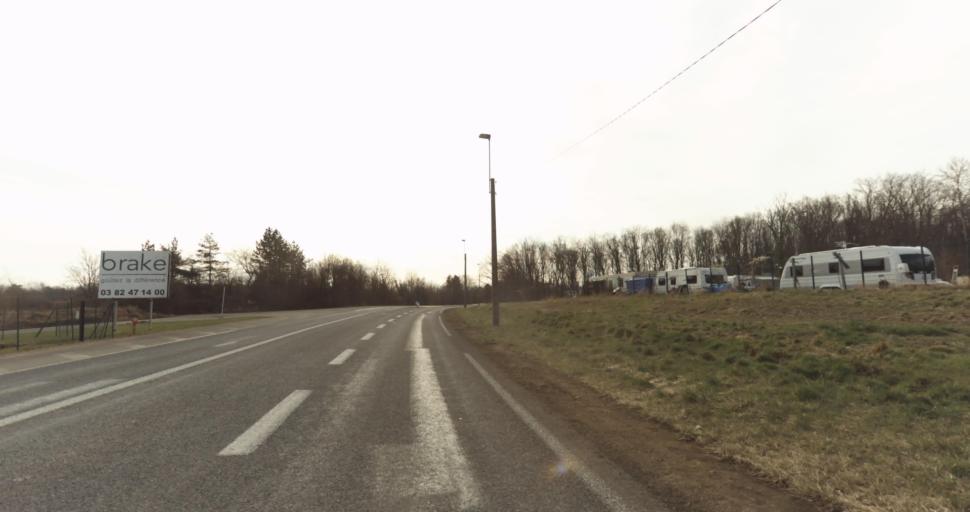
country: FR
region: Lorraine
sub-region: Departement de Meurthe-et-Moselle
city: Jarny
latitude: 49.1373
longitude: 5.8920
